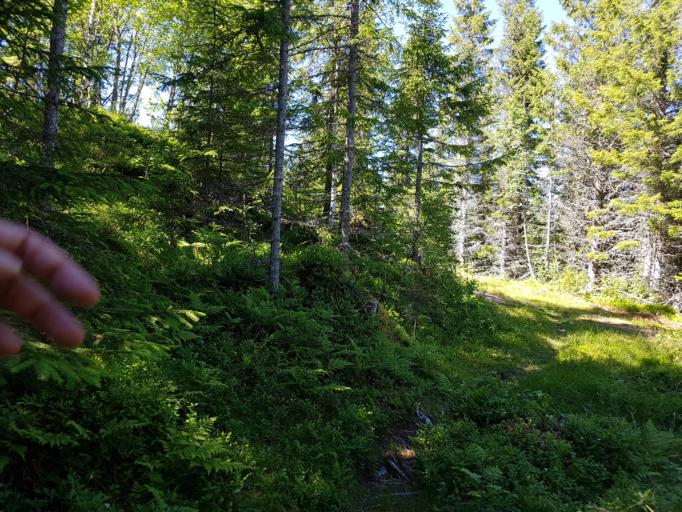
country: NO
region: Sor-Trondelag
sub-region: Melhus
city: Melhus
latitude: 63.4394
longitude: 10.2086
